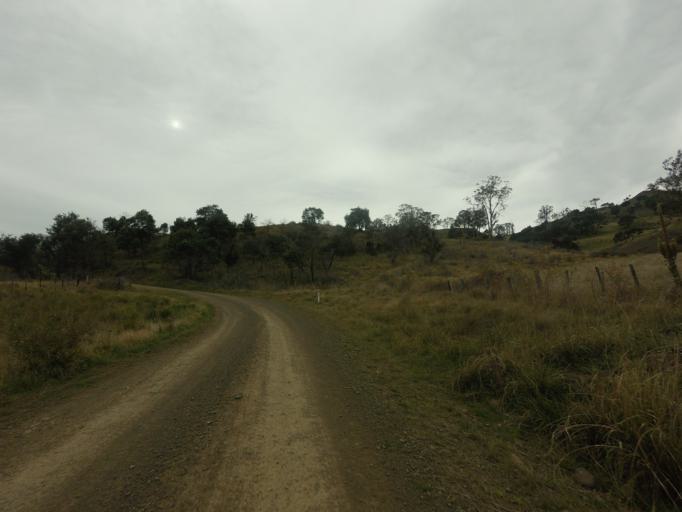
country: AU
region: Tasmania
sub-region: Derwent Valley
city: New Norfolk
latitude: -42.3631
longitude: 146.8428
